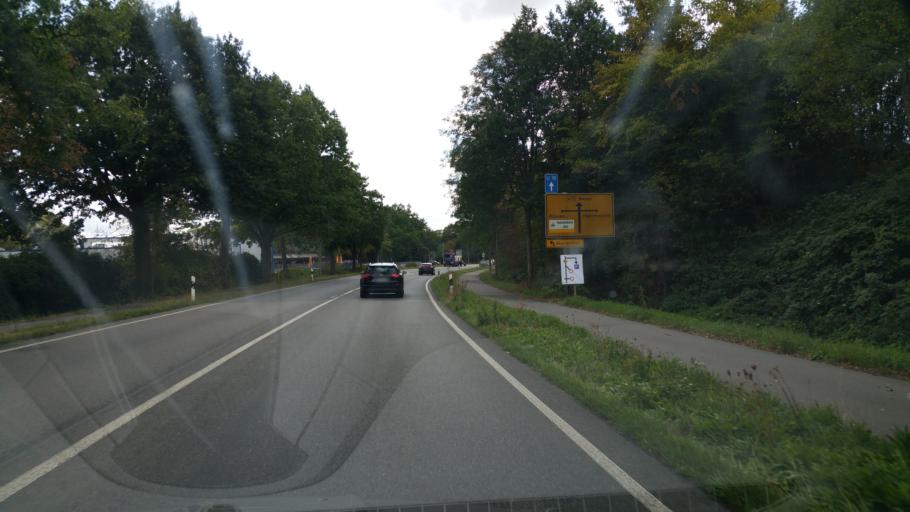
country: DE
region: North Rhine-Westphalia
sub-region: Regierungsbezirk Dusseldorf
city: Hamminkeln
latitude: 51.7310
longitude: 6.6011
